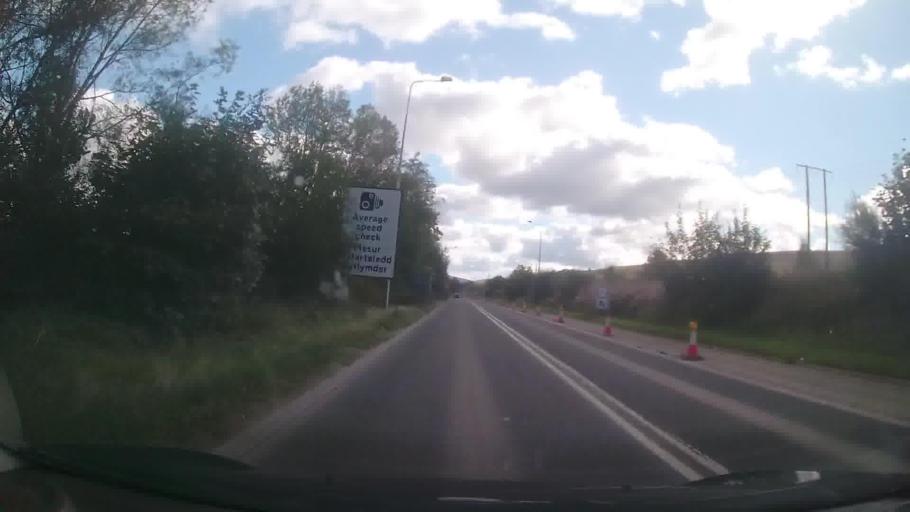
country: GB
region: Wales
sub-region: Rhondda Cynon Taf
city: Hirwaun
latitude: 51.7358
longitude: -3.5114
